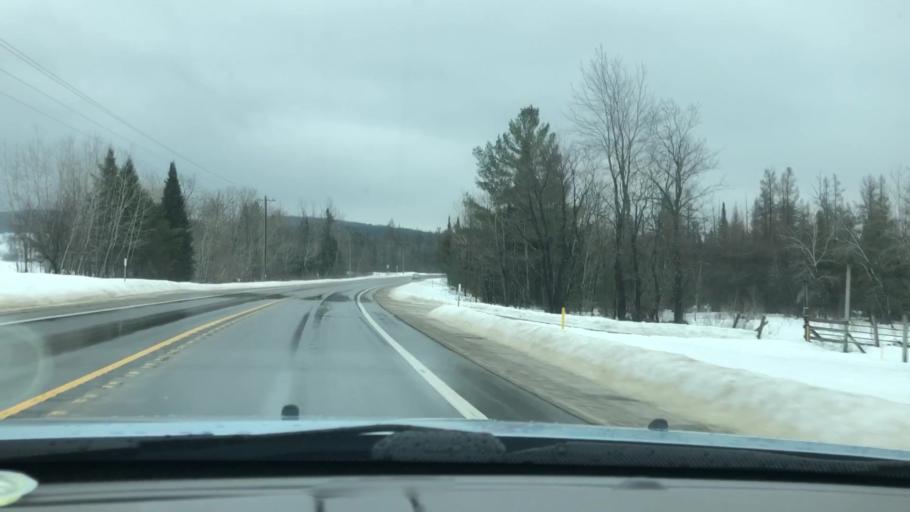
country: US
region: Michigan
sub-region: Charlevoix County
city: Boyne City
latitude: 45.0937
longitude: -84.9513
